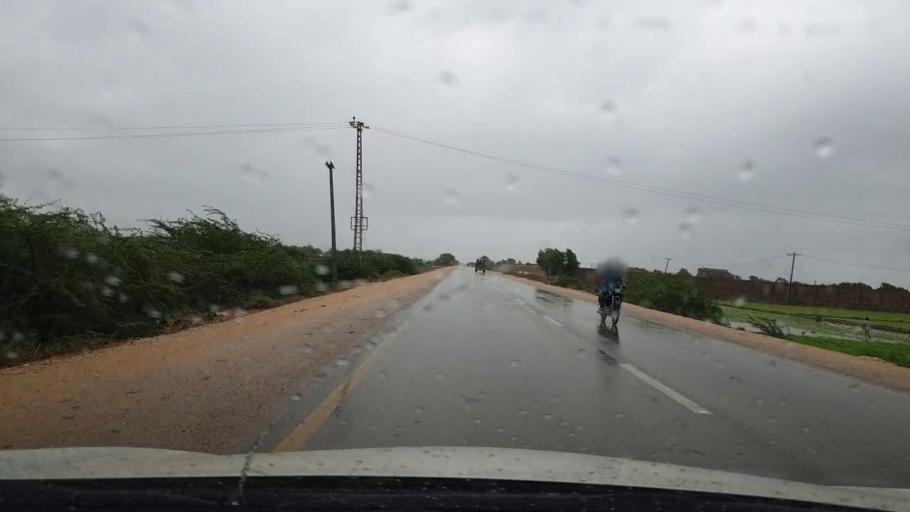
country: PK
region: Sindh
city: Kario
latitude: 24.6534
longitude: 68.5707
